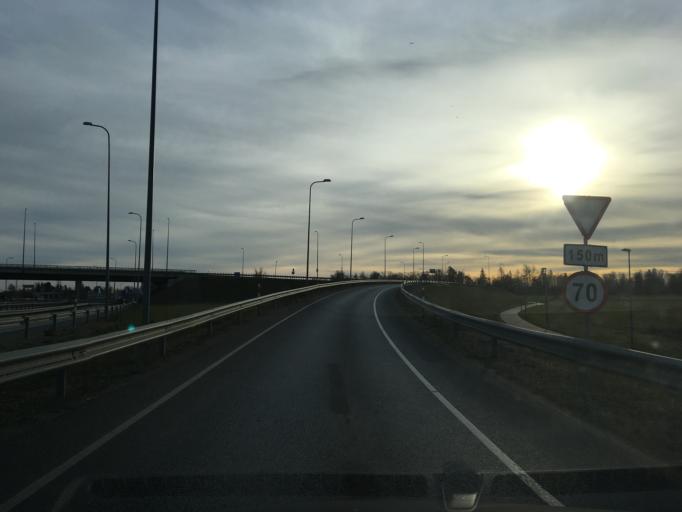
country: EE
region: Ida-Virumaa
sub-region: Johvi vald
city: Johvi
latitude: 59.3692
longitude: 27.3883
